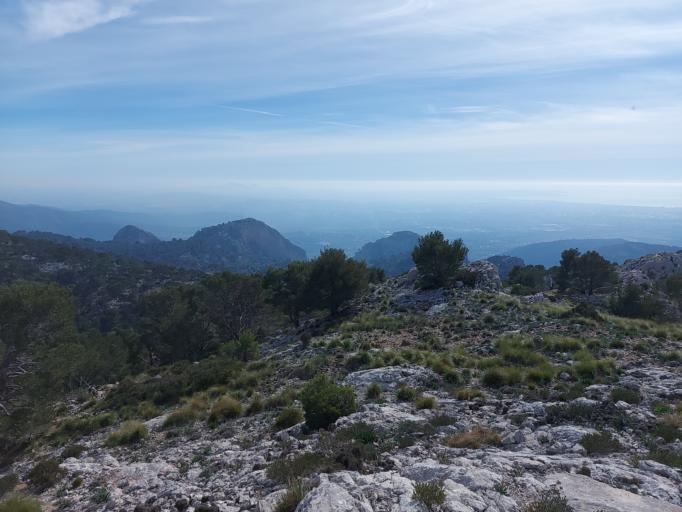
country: ES
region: Balearic Islands
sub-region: Illes Balears
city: Valldemossa
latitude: 39.7094
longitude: 2.6570
